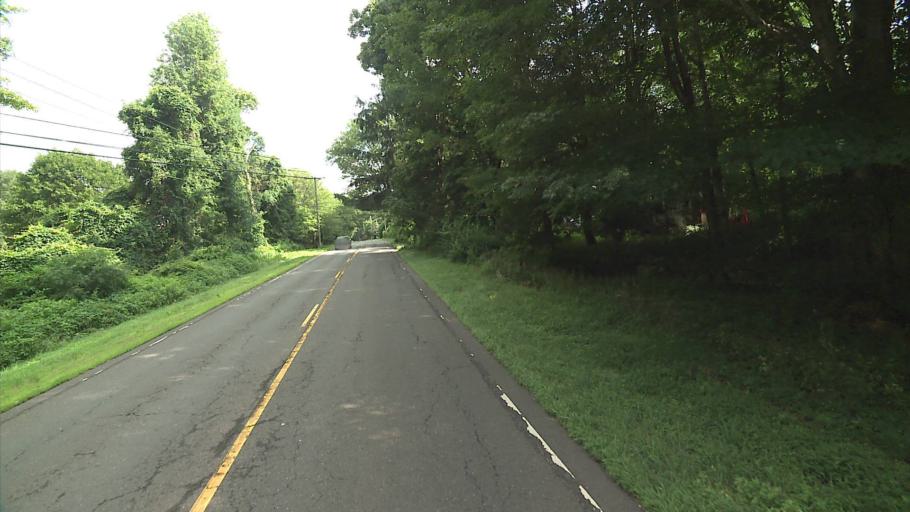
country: US
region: Connecticut
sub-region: Middlesex County
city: Clinton
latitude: 41.3049
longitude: -72.4916
